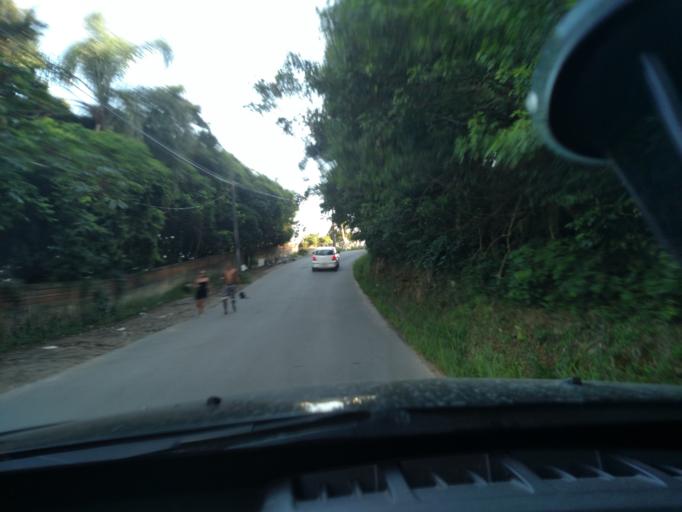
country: BR
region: Santa Catarina
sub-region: Porto Belo
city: Porto Belo
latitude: -27.1465
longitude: -48.4806
